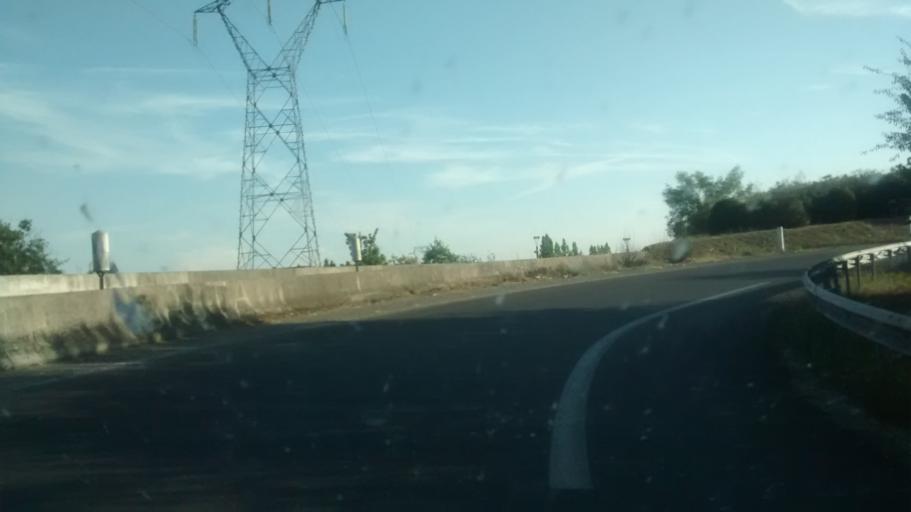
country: FR
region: Midi-Pyrenees
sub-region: Departement de la Haute-Garonne
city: Pinsaguel
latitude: 43.5151
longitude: 1.3806
